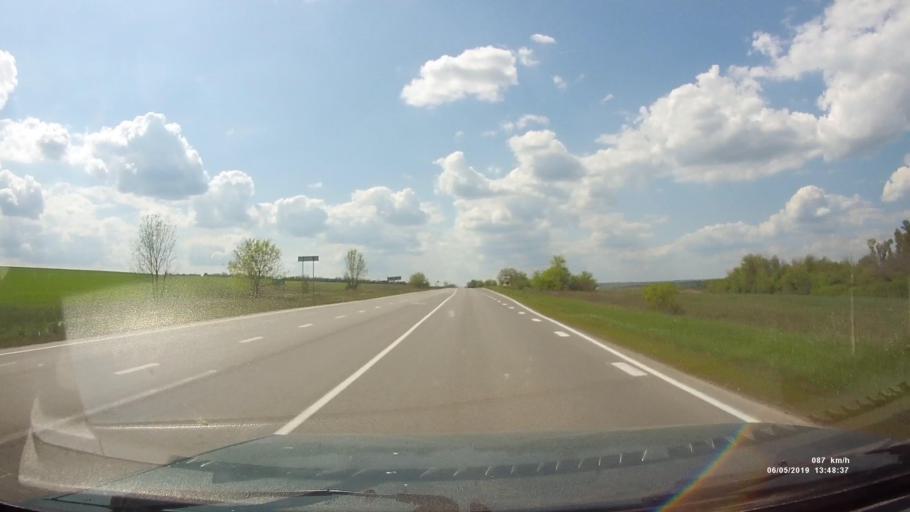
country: RU
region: Rostov
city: Melikhovskaya
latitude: 47.6586
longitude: 40.5404
